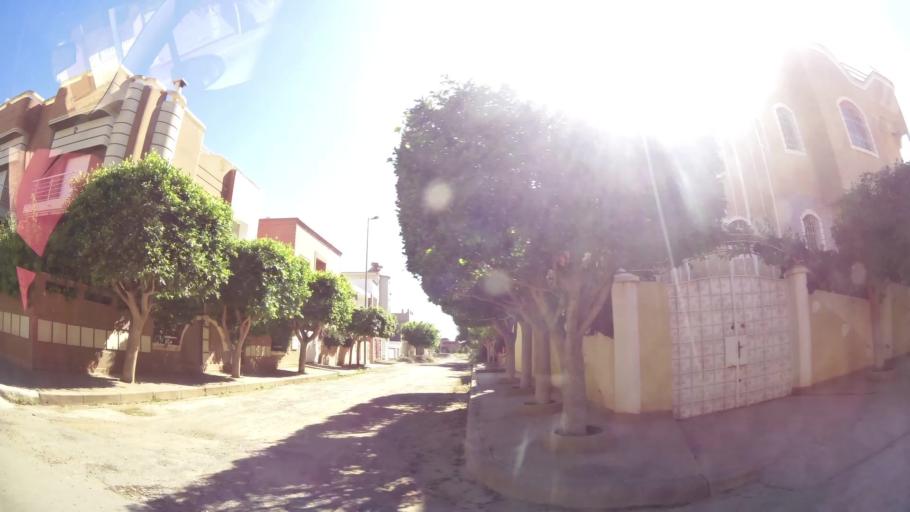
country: MA
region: Oriental
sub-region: Berkane-Taourirt
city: Berkane
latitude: 34.9442
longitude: -2.3345
